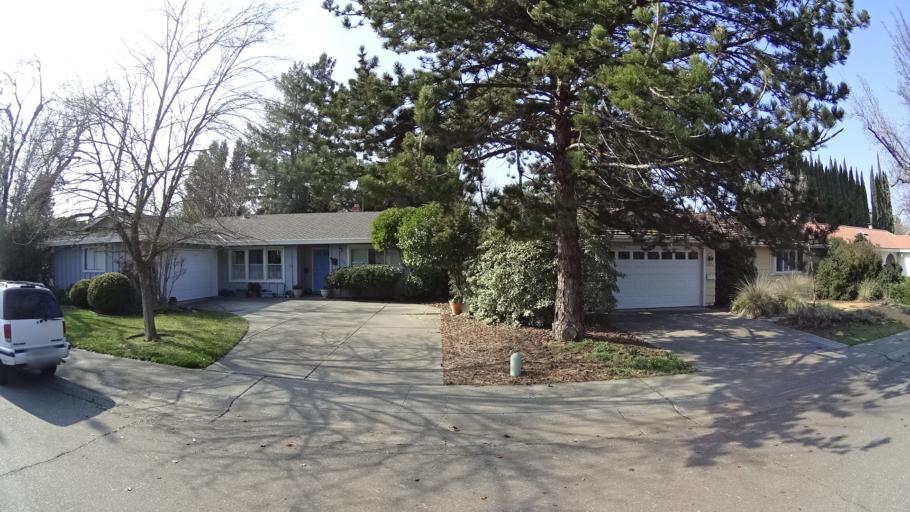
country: US
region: California
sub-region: Yolo County
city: Davis
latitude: 38.5521
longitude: -121.7716
